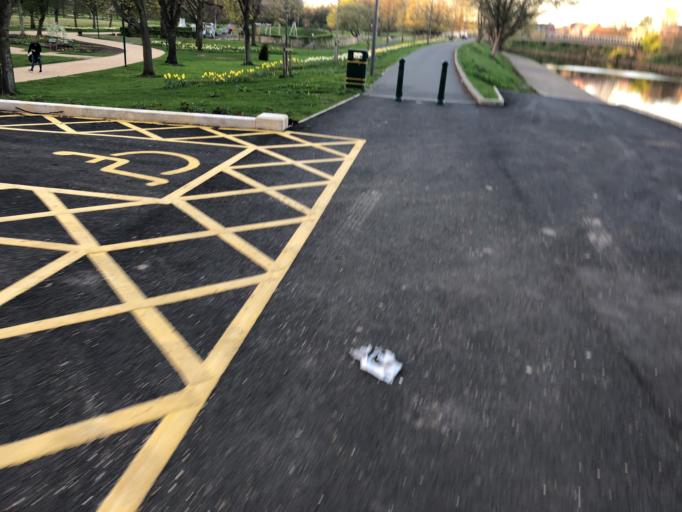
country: GB
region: England
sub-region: City and Borough of Salford
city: Salford
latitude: 53.4858
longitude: -2.2703
